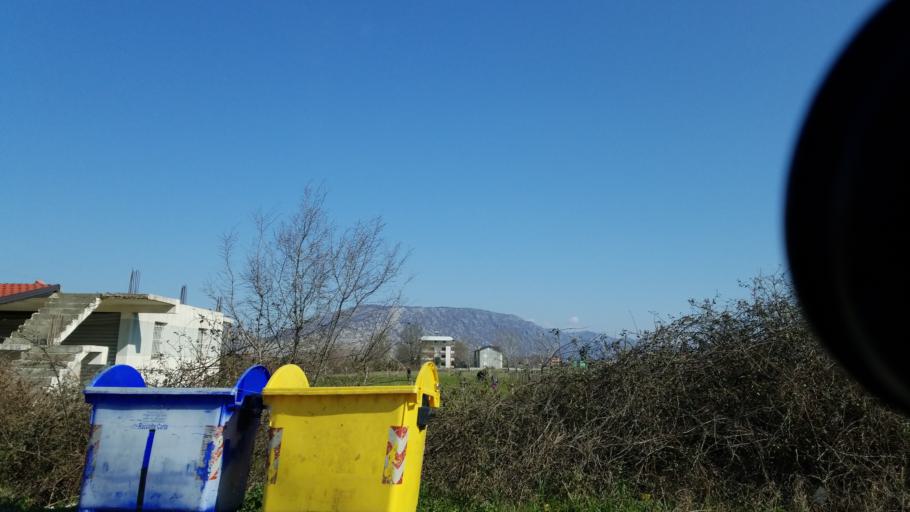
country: AL
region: Shkoder
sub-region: Rrethi i Shkodres
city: Velipoje
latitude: 41.8716
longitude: 19.4042
